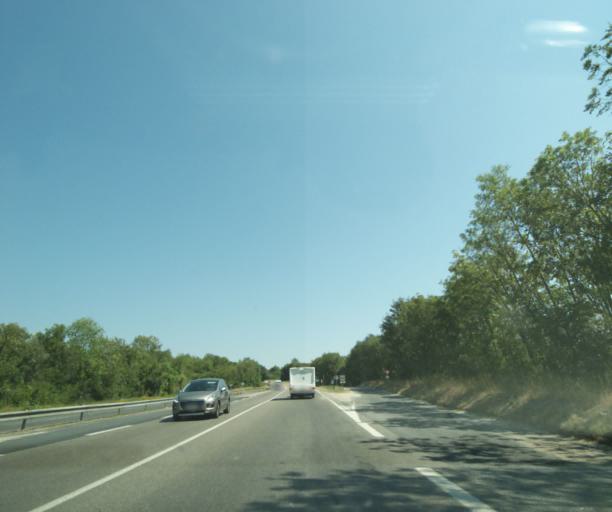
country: FR
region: Champagne-Ardenne
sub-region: Departement de la Marne
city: Vitry-le-Francois
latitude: 48.7431
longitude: 4.5933
